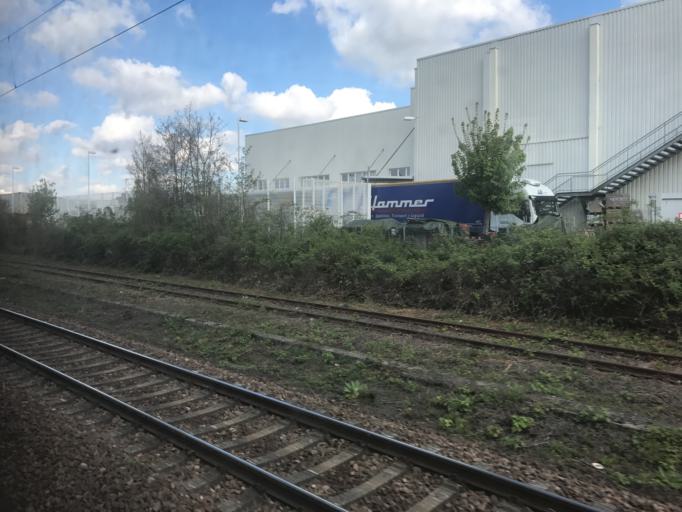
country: DE
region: Rheinland-Pfalz
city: Gartenstadt
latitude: 49.4872
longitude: 8.4063
